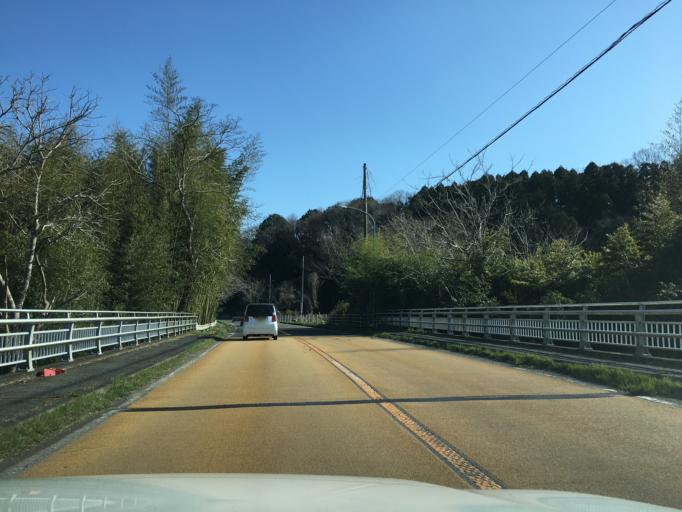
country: JP
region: Ibaraki
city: Mito-shi
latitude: 36.4424
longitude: 140.4122
